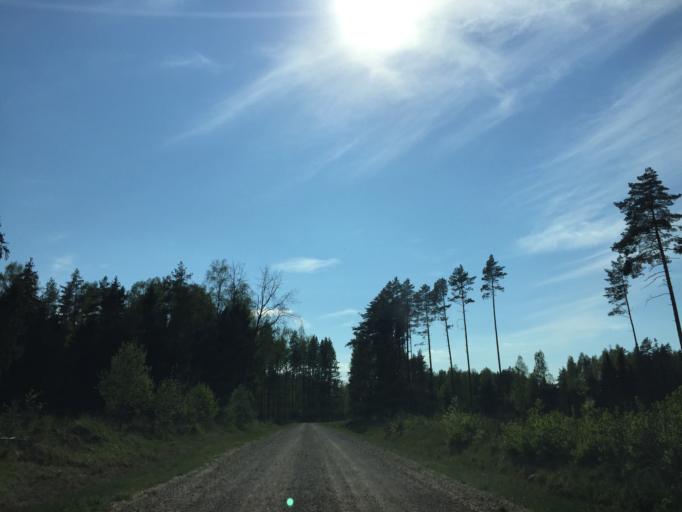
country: LV
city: Tireli
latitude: 56.8188
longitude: 23.6969
